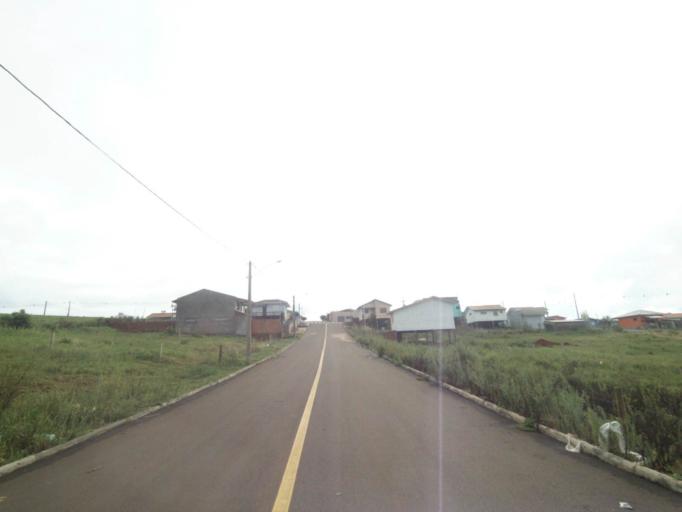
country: BR
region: Rio Grande do Sul
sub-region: Lagoa Vermelha
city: Lagoa Vermelha
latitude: -28.2260
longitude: -51.5207
